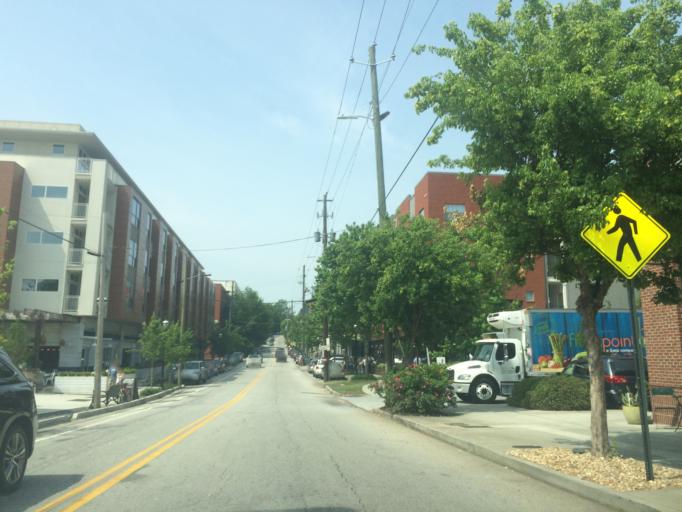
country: US
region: Georgia
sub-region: DeKalb County
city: Druid Hills
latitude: 33.7629
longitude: -84.3582
